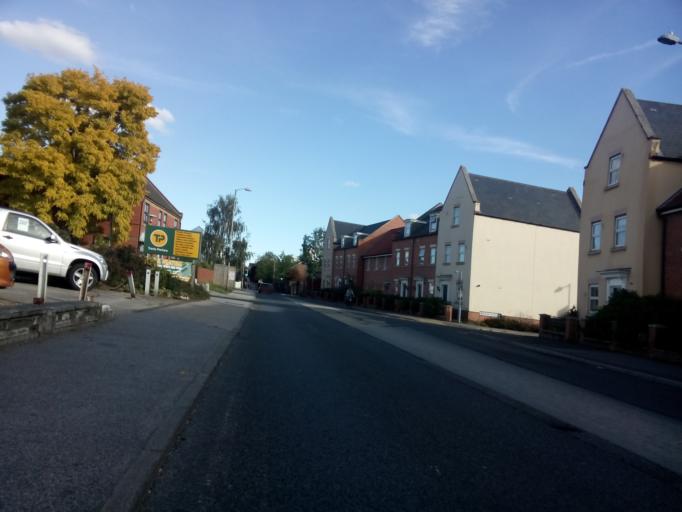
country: GB
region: England
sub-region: Suffolk
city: Ipswich
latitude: 52.0580
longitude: 1.1388
